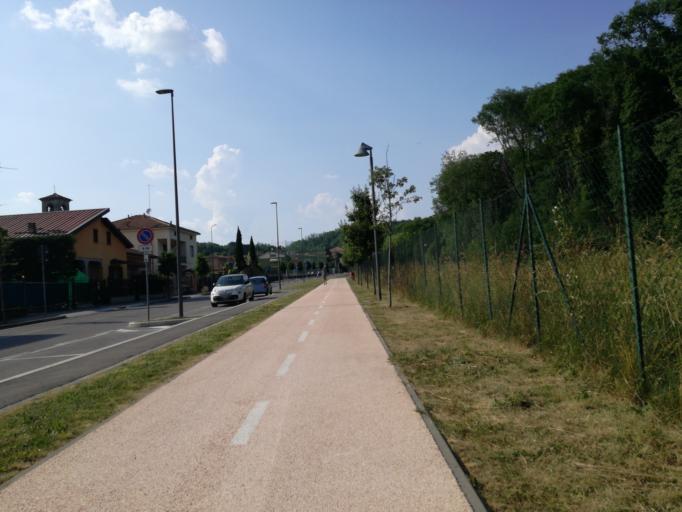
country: IT
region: Lombardy
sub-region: Provincia di Bergamo
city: Calusco d'Adda
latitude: 45.6926
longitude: 9.4679
